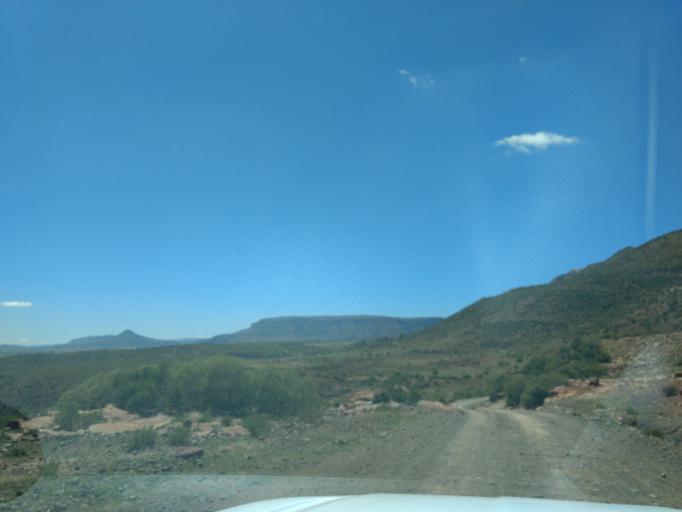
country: LS
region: Maseru
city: Maseru
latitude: -29.4530
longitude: 27.3693
